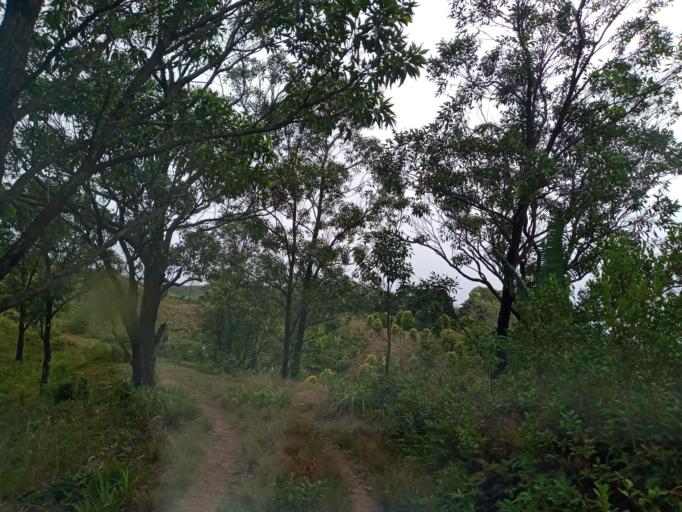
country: MG
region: Atsimo-Atsinanana
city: Vohipaho
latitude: -23.9960
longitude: 47.4025
